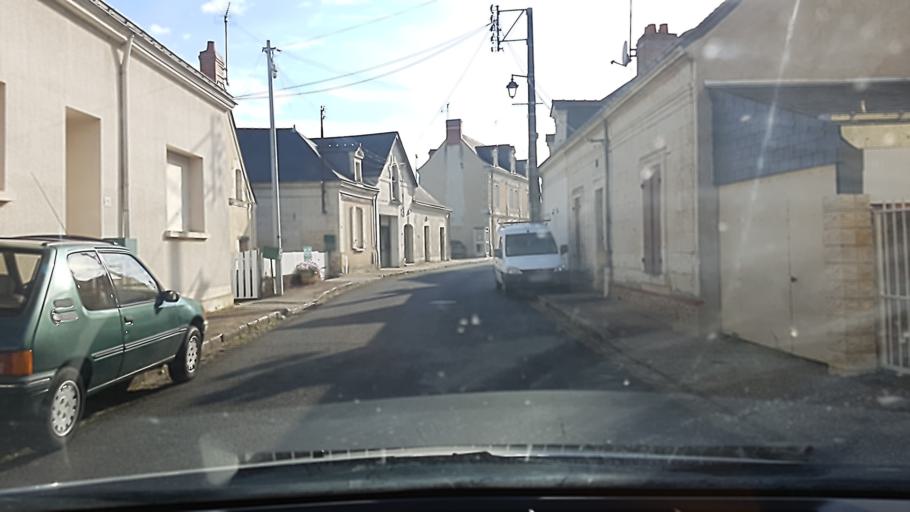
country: FR
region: Pays de la Loire
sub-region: Departement de Maine-et-Loire
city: Maze
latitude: 47.5021
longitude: -0.2461
